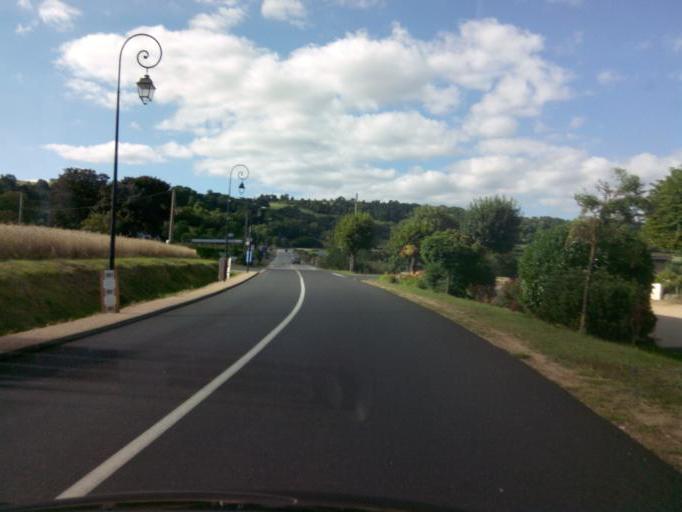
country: FR
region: Auvergne
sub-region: Departement de la Haute-Loire
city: Saint-Paulien
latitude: 45.1410
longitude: 3.8154
